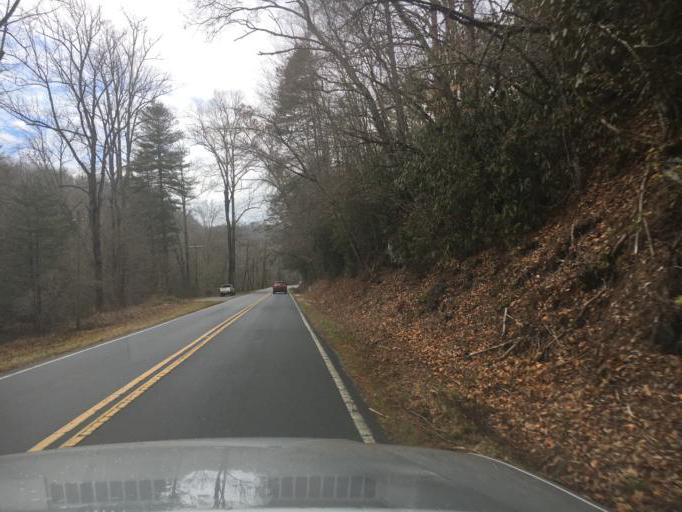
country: US
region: North Carolina
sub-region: Transylvania County
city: Brevard
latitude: 35.2747
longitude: -82.7078
